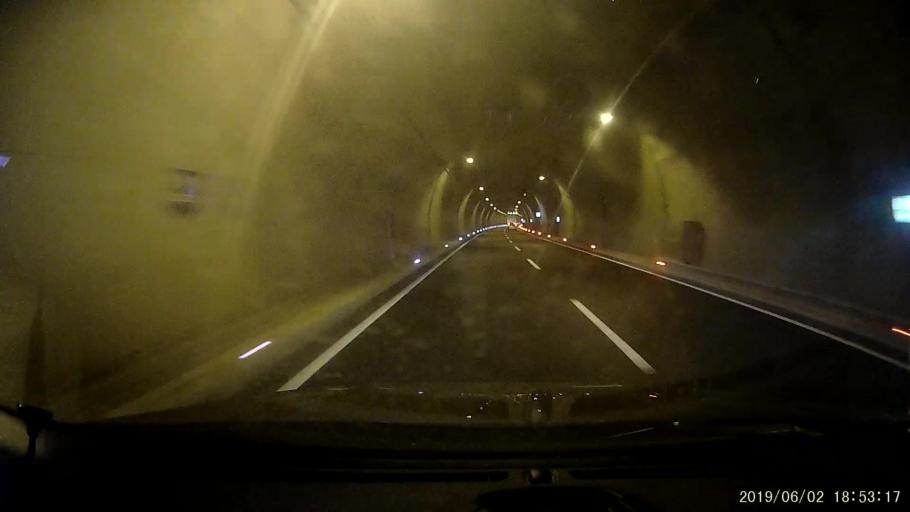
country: TR
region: Ordu
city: Ordu
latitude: 40.9807
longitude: 37.8290
